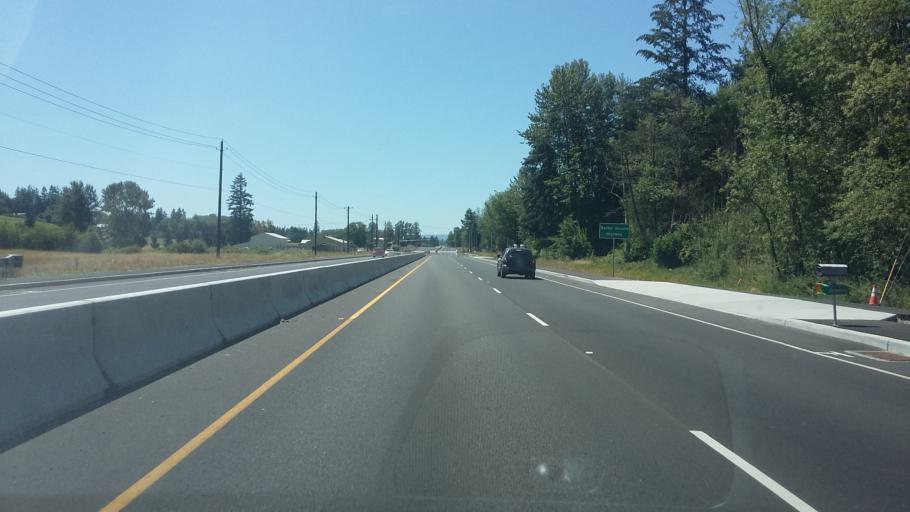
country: US
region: Washington
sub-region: Clark County
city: Meadow Glade
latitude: 45.7805
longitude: -122.5737
